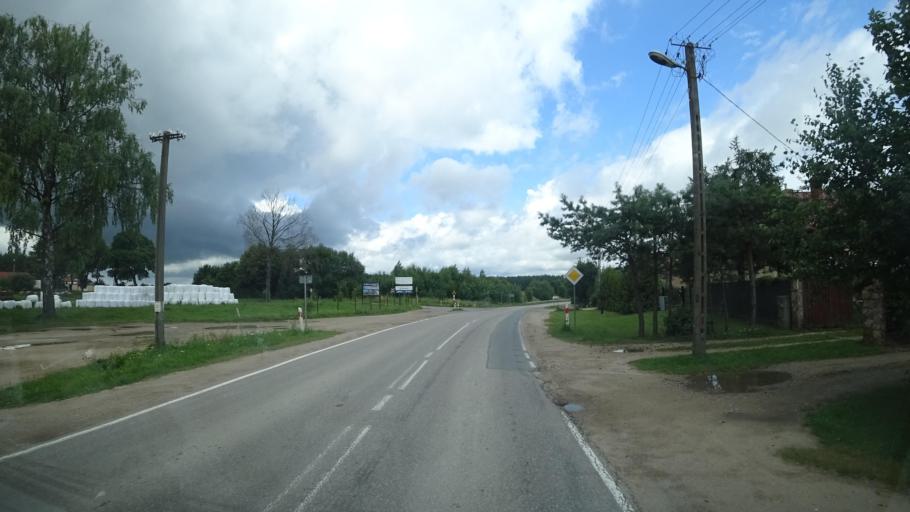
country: PL
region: Warmian-Masurian Voivodeship
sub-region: Powiat olecki
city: Kowale Oleckie
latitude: 54.1033
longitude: 22.4353
